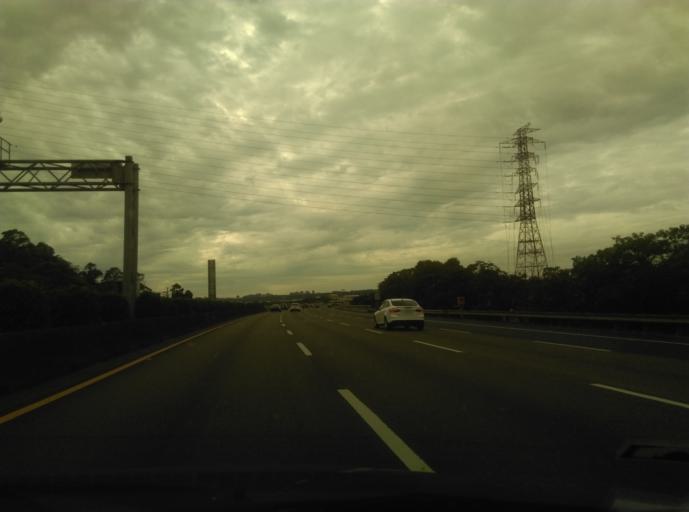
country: TW
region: Taiwan
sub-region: Taoyuan
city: Taoyuan
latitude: 24.9351
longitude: 121.3526
